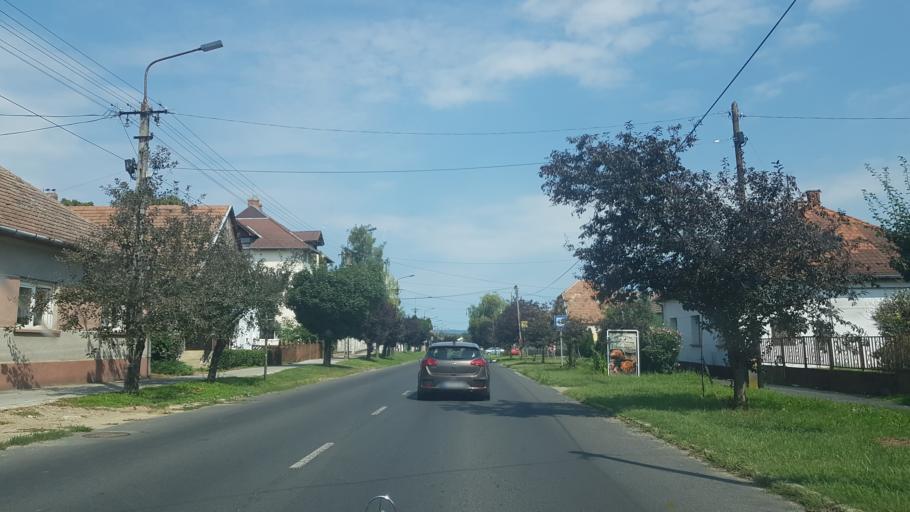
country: HU
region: Somogy
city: Kethely
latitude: 46.6462
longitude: 17.3935
